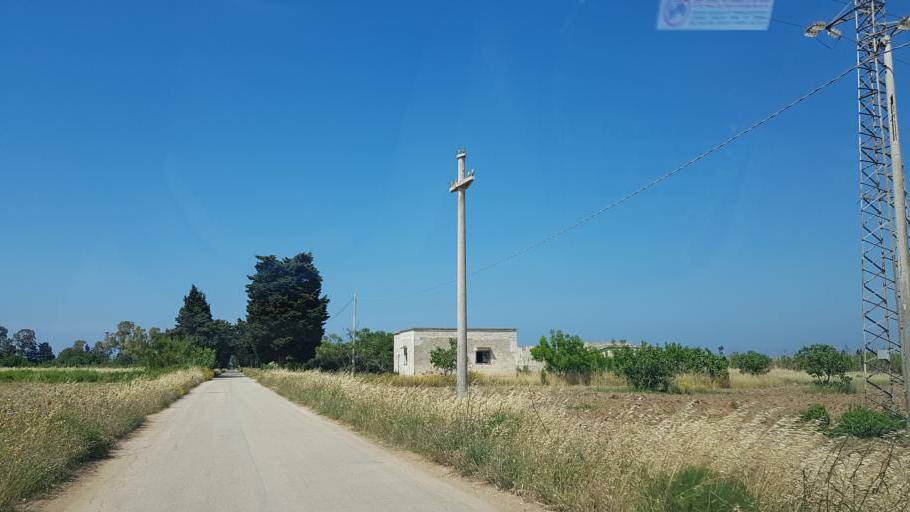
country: IT
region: Apulia
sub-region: Provincia di Brindisi
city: Brindisi
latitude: 40.6617
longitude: 17.8605
